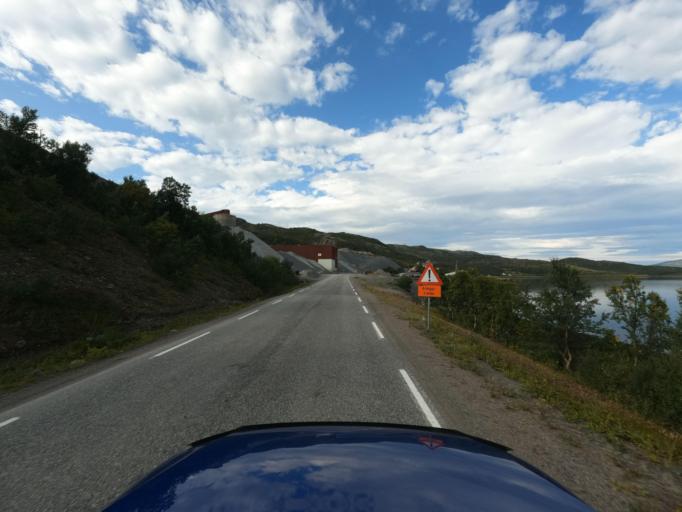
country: NO
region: Finnmark Fylke
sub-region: Kvalsund
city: Kvalsund
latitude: 70.4514
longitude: 24.2935
